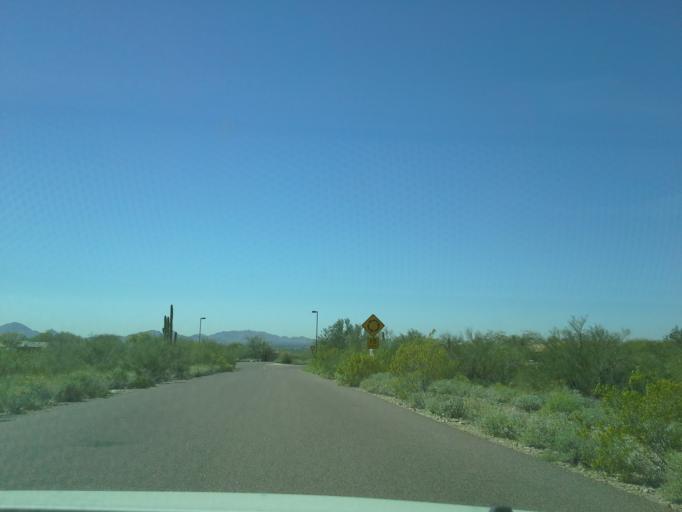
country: US
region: Arizona
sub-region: Maricopa County
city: Fountain Hills
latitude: 33.5978
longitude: -111.8154
